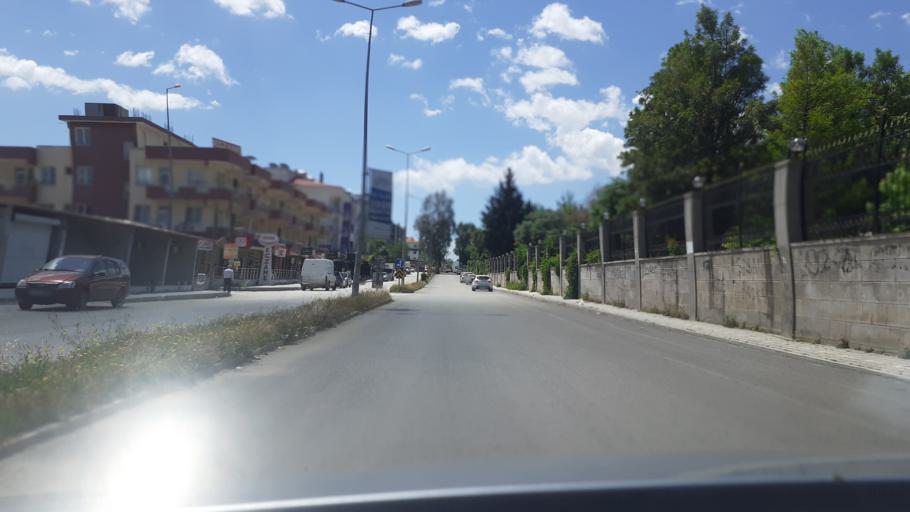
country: TR
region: Hatay
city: Anayazi
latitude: 36.3308
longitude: 36.1993
